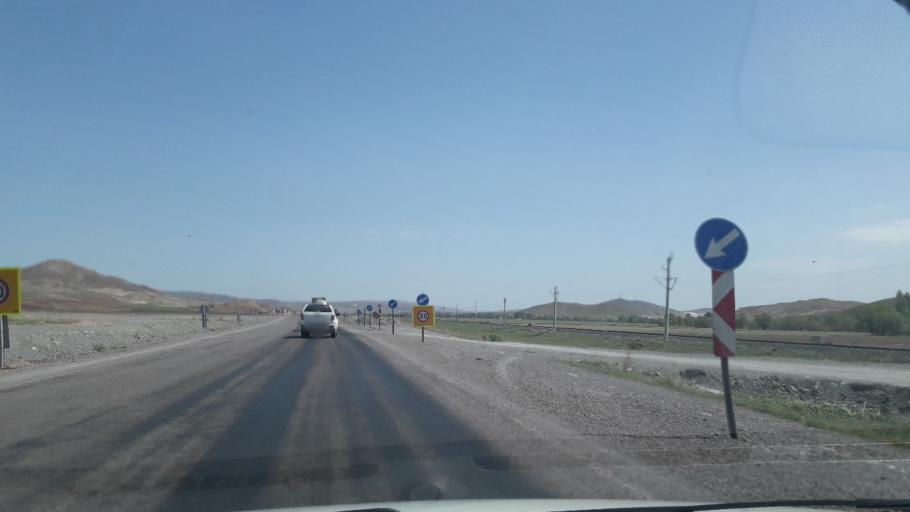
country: TR
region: Sivas
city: Ulas
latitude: 39.5259
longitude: 37.0123
